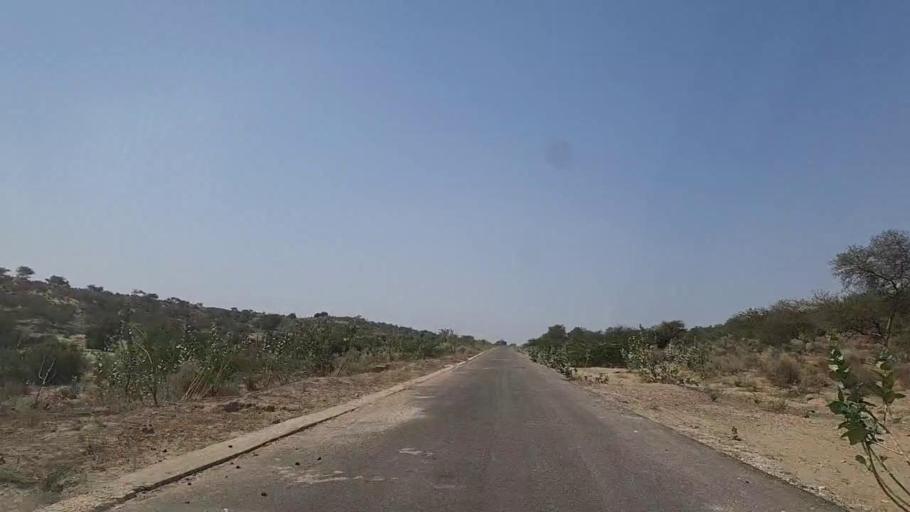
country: PK
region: Sindh
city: Diplo
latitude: 24.5722
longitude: 69.4762
